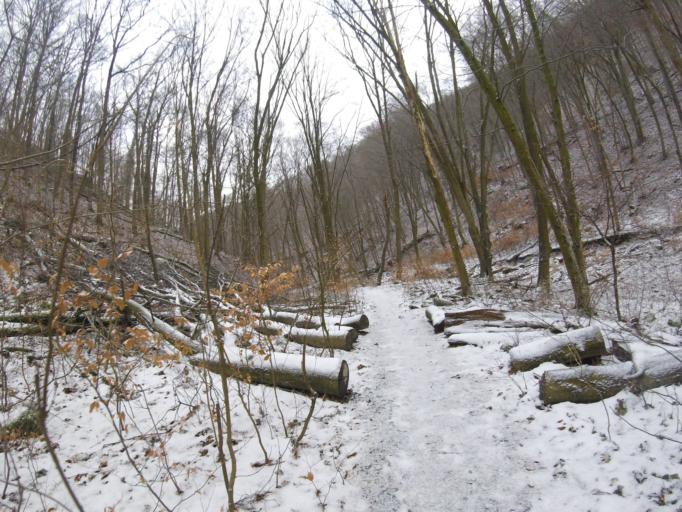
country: HU
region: Pest
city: Visegrad
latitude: 47.7431
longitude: 18.9978
